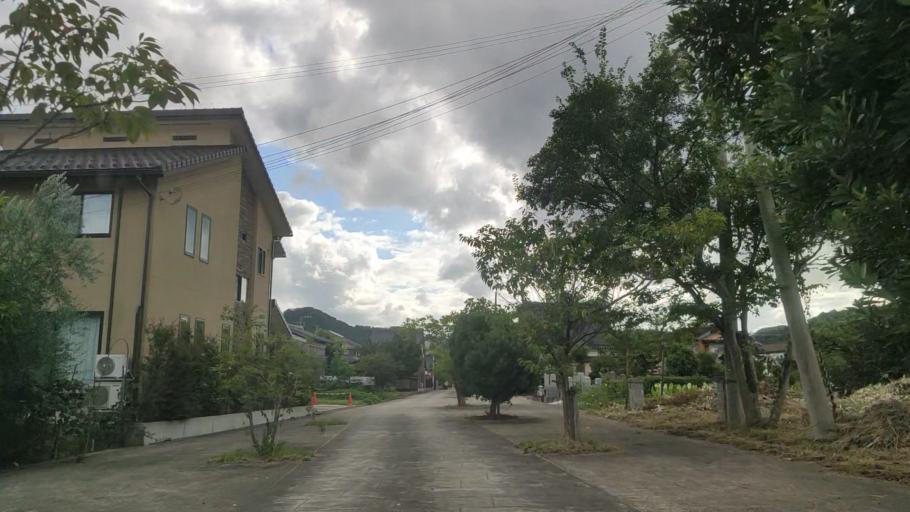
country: JP
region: Hyogo
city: Toyooka
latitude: 35.6077
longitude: 134.8979
